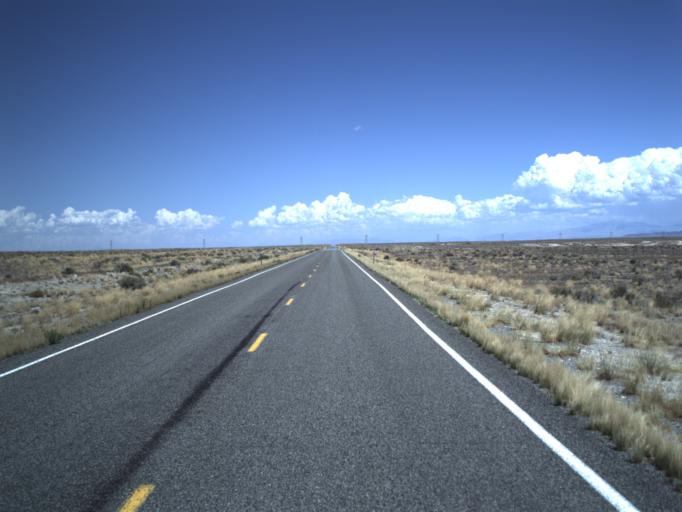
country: US
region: Utah
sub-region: Millard County
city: Delta
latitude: 39.1611
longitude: -113.0506
